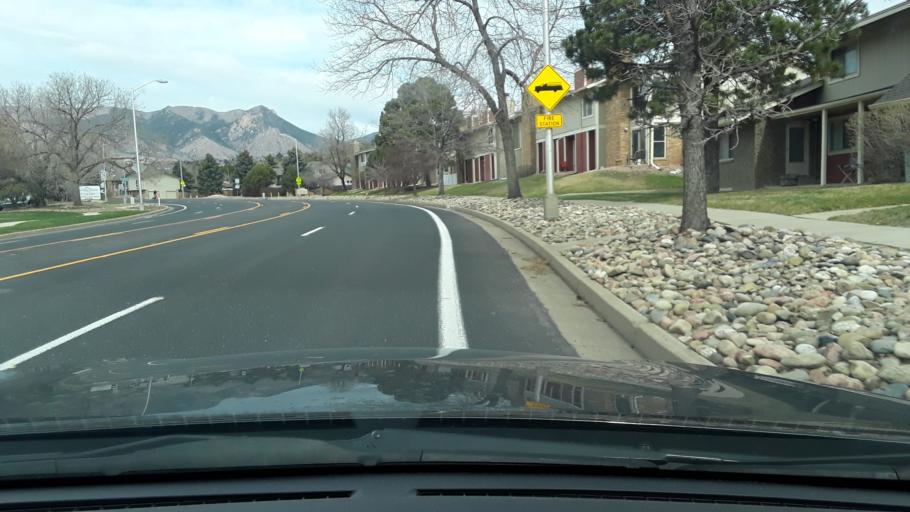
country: US
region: Colorado
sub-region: El Paso County
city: Air Force Academy
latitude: 38.9287
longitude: -104.8336
